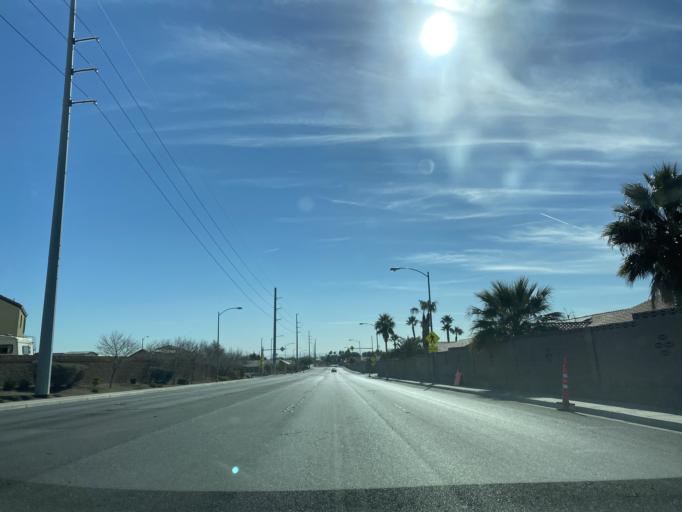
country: US
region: Nevada
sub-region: Clark County
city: North Las Vegas
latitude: 36.2517
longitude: -115.1441
